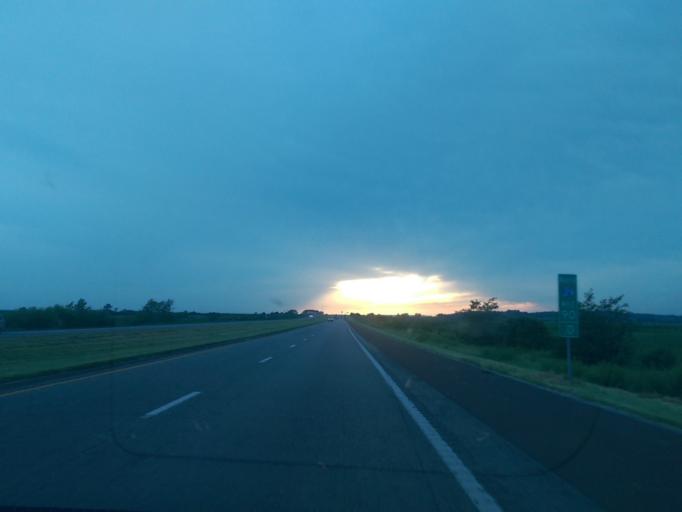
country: US
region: Missouri
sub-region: Holt County
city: Mound City
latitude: 40.1826
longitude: -95.3206
